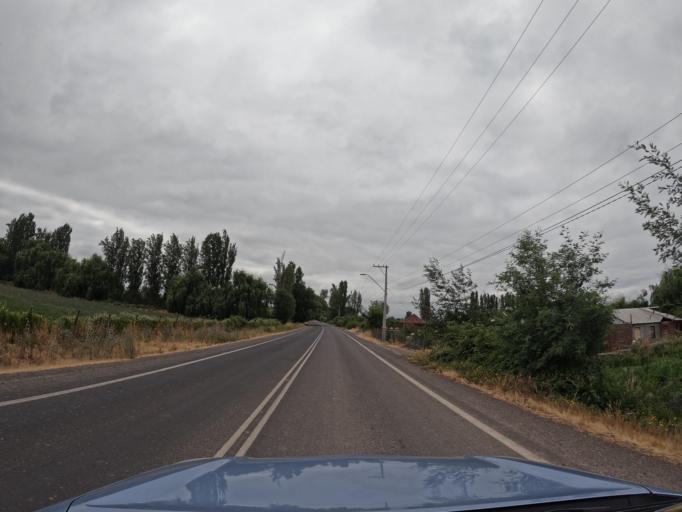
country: CL
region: O'Higgins
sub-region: Provincia de Colchagua
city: Chimbarongo
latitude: -34.7332
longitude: -71.0714
